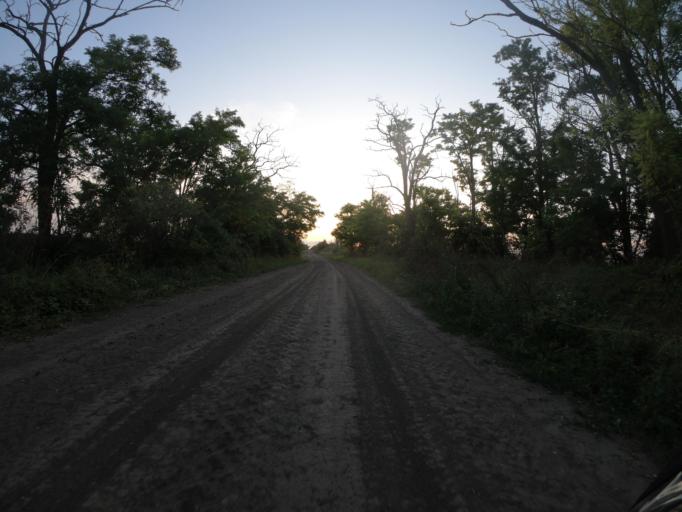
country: HU
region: Borsod-Abauj-Zemplen
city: Szentistvan
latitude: 47.7467
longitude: 20.7187
